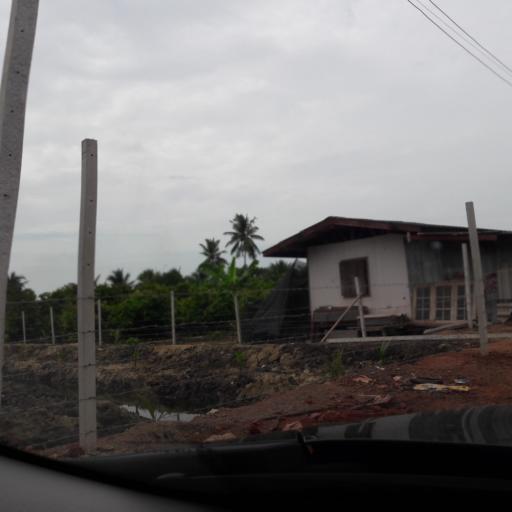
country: TH
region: Ratchaburi
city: Damnoen Saduak
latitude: 13.5729
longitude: 99.9444
